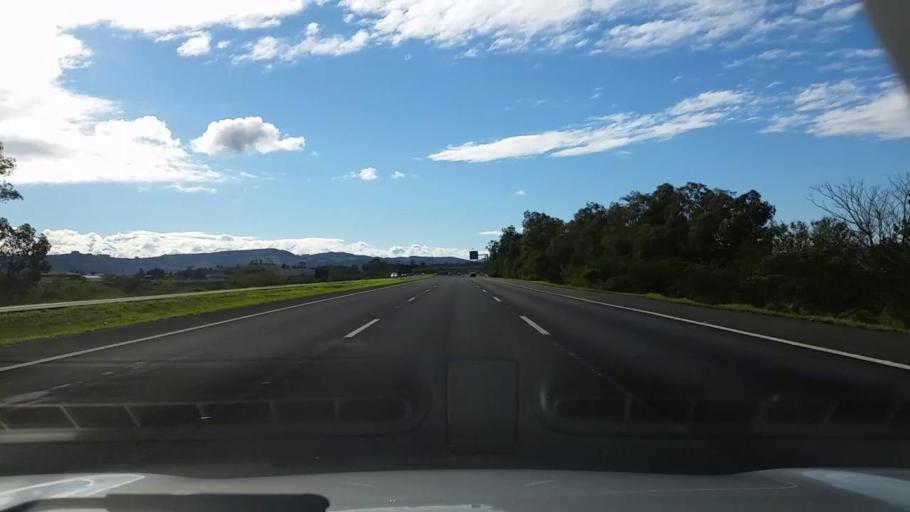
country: BR
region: Rio Grande do Sul
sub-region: Rolante
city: Rolante
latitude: -29.8809
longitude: -50.5192
